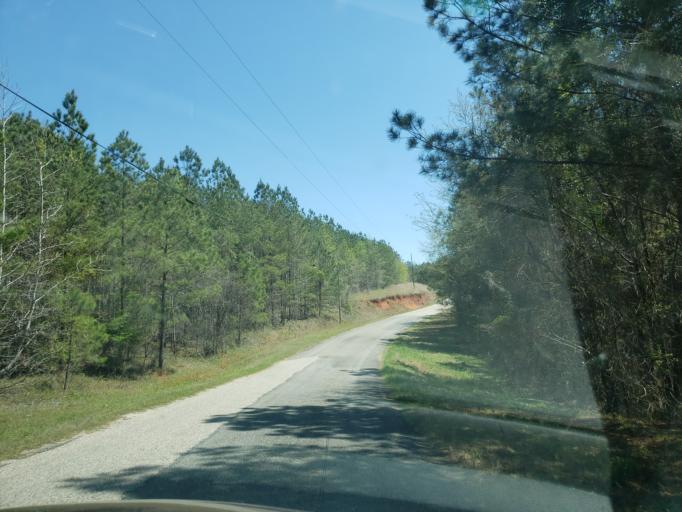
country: US
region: Alabama
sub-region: Elmore County
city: Tallassee
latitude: 32.6698
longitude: -85.8406
